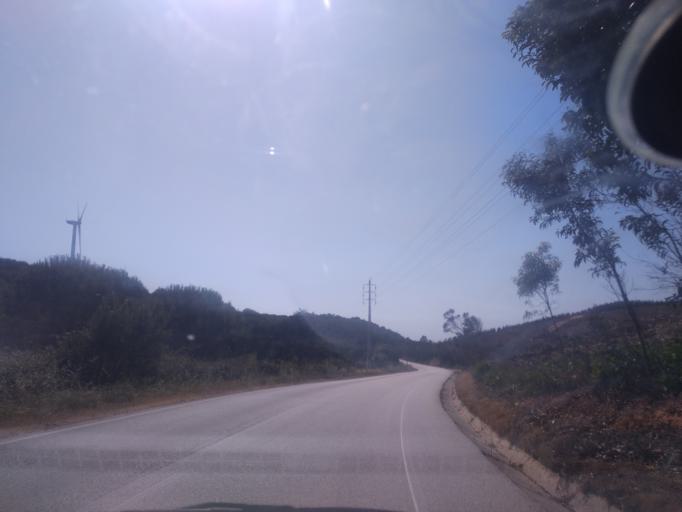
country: PT
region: Faro
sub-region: Aljezur
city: Aljezur
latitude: 37.2152
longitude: -8.7839
